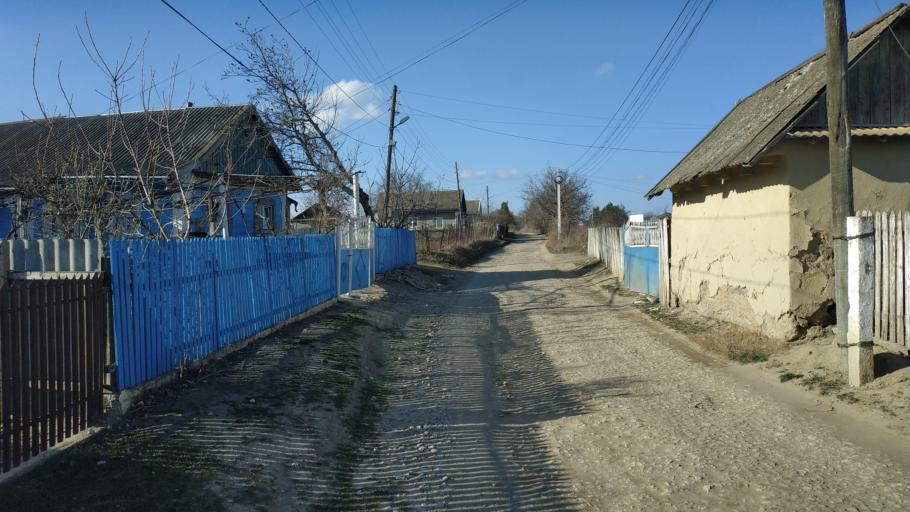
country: MD
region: Hincesti
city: Hincesti
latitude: 46.7334
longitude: 28.5119
